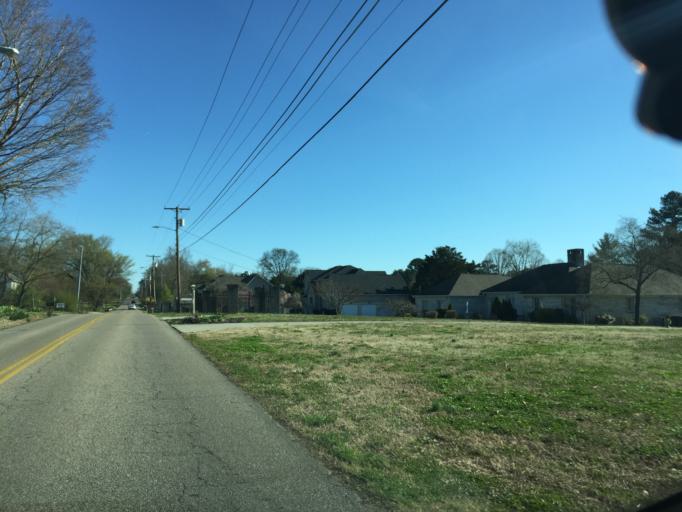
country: US
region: Tennessee
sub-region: Hamilton County
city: East Brainerd
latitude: 35.0340
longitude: -85.1729
